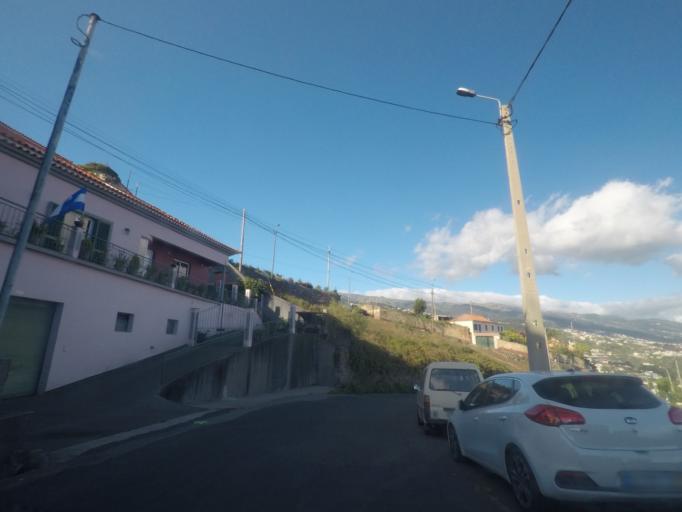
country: PT
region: Madeira
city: Camara de Lobos
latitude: 32.6645
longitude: -16.9918
